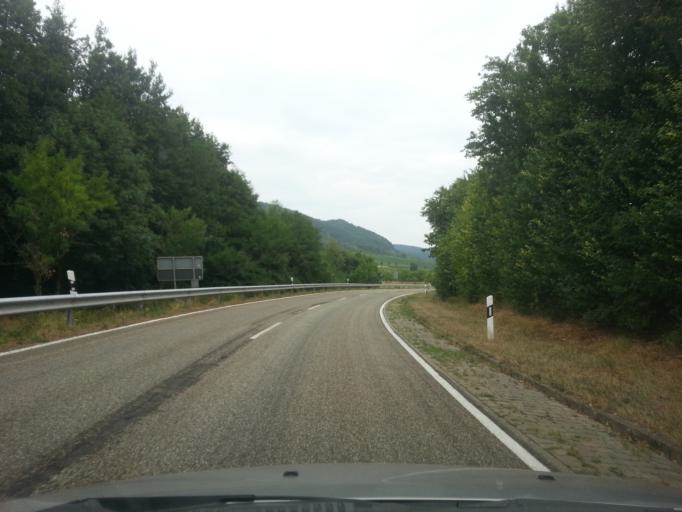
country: DE
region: Rheinland-Pfalz
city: Siebeldingen
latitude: 49.2178
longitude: 8.0500
